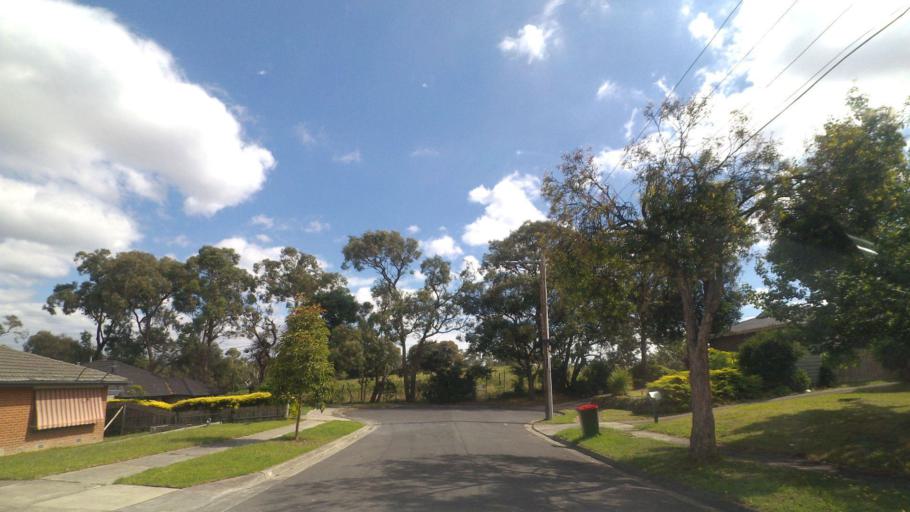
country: AU
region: Victoria
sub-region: Knox
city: Bayswater
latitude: -37.8663
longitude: 145.2584
